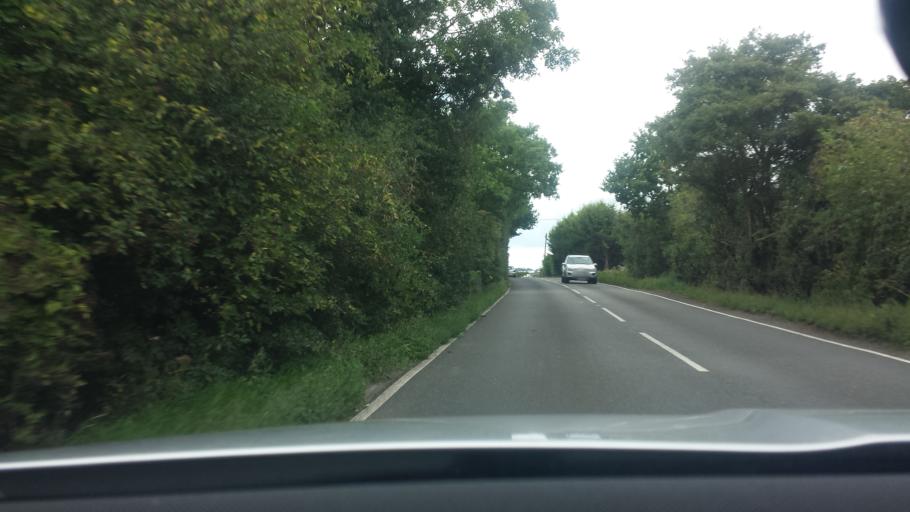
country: GB
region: England
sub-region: Kent
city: Staplehurst
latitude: 51.1932
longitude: 0.5336
